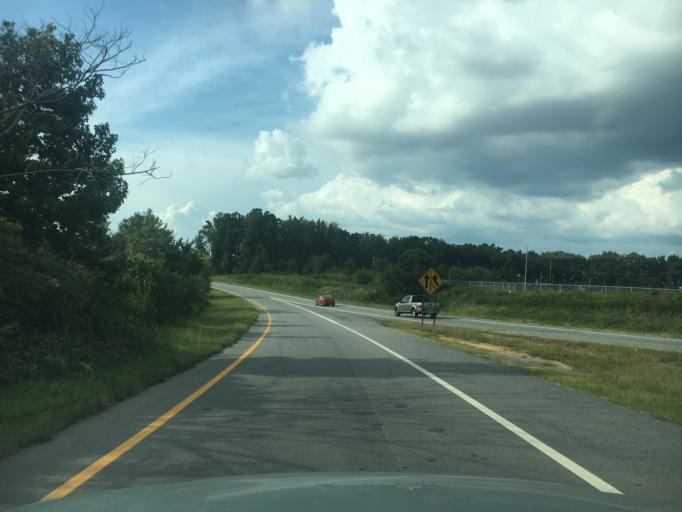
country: US
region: South Carolina
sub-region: Greenville County
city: Greer
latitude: 34.8877
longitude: -82.1915
